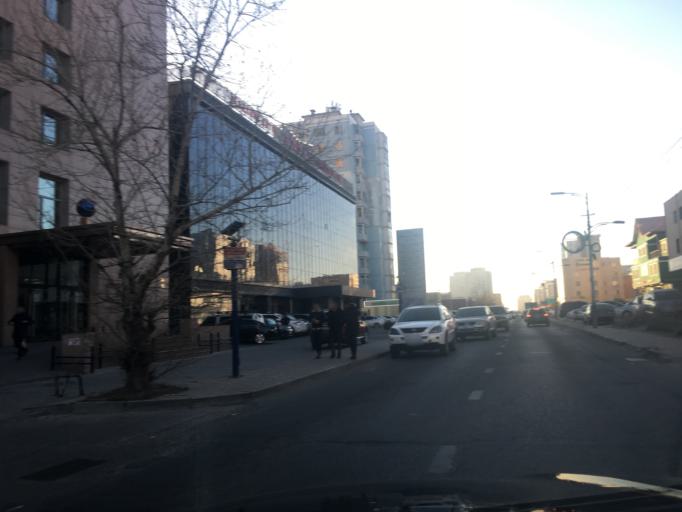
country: MN
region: Ulaanbaatar
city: Ulaanbaatar
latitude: 47.9184
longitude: 106.8840
